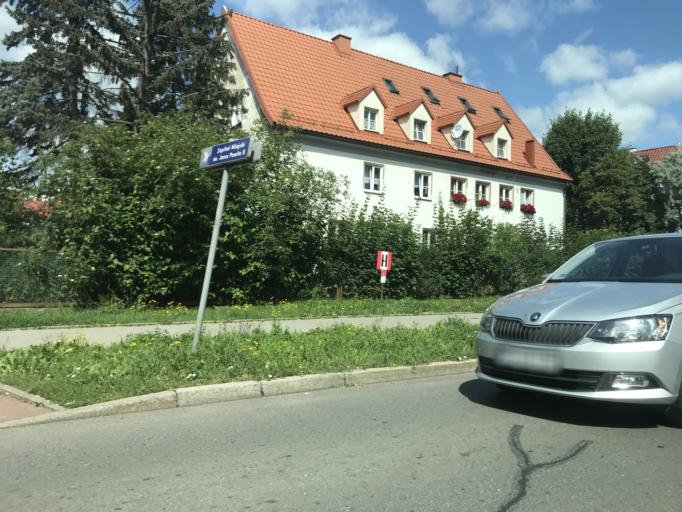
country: PL
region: Warmian-Masurian Voivodeship
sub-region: Powiat elblaski
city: Elblag
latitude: 54.1574
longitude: 19.4209
